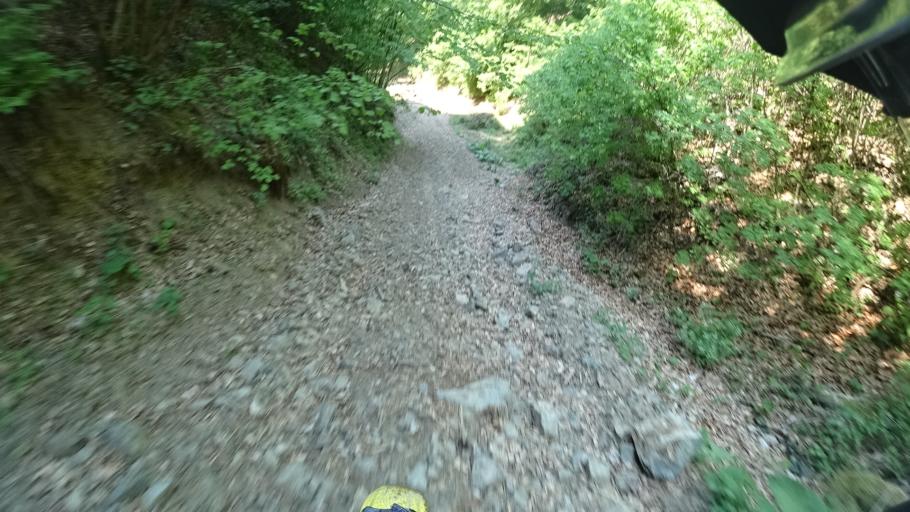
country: HR
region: Grad Zagreb
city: Kasina
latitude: 45.9440
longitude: 15.9871
